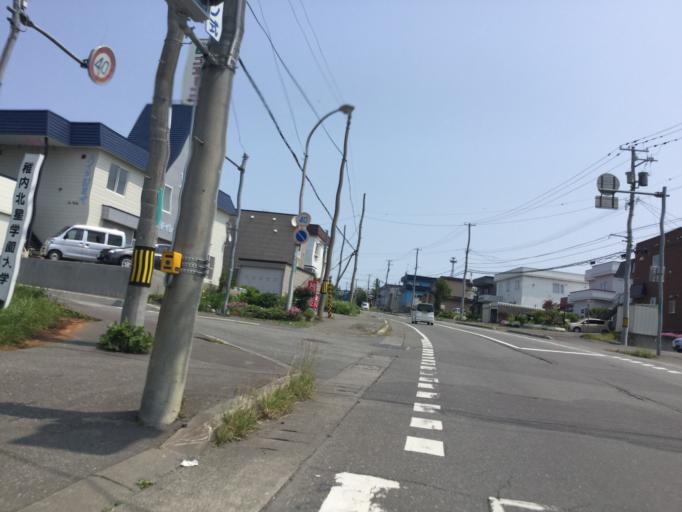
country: JP
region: Hokkaido
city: Wakkanai
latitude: 45.3866
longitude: 141.7175
